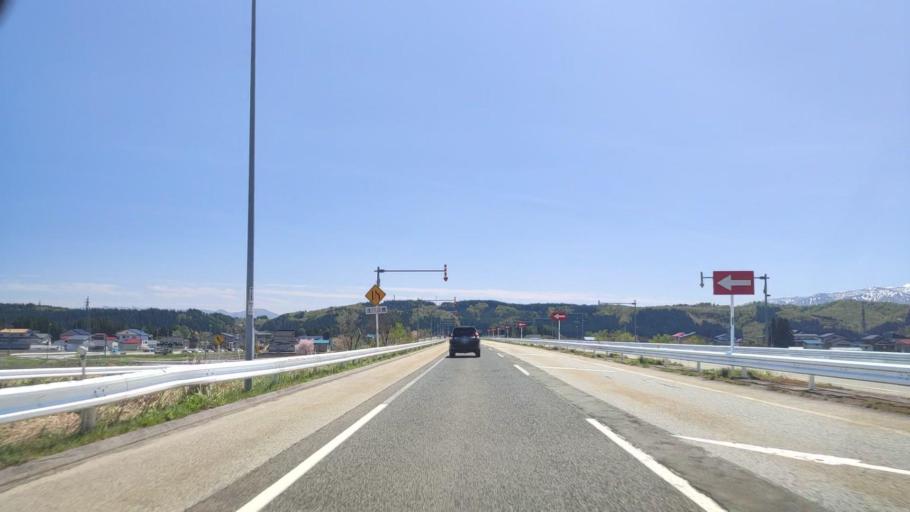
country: JP
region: Yamagata
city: Shinjo
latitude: 38.7048
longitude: 140.3092
